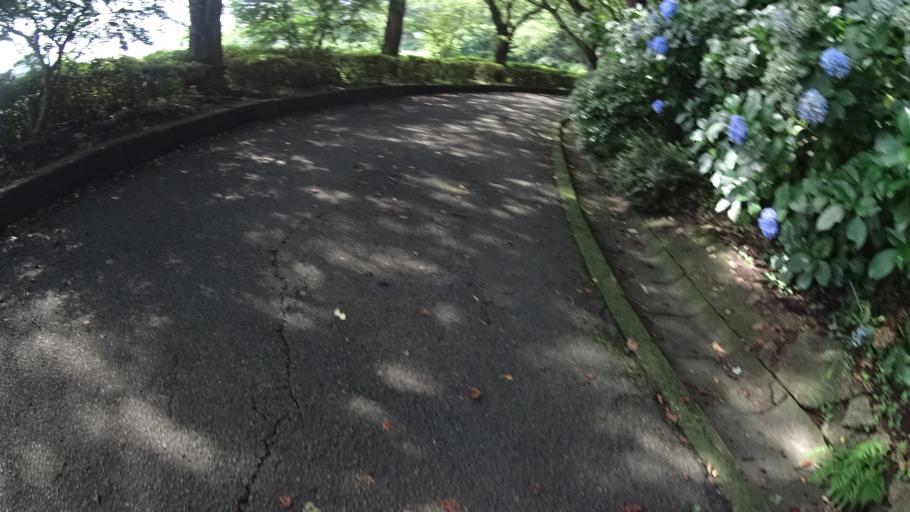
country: JP
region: Kanagawa
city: Zushi
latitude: 35.3079
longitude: 139.6128
